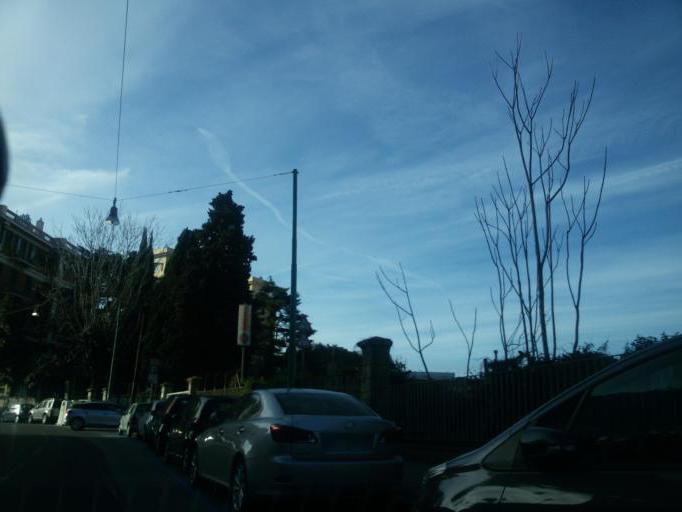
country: IT
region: Liguria
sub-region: Provincia di Genova
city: San Teodoro
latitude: 44.3944
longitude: 8.9552
